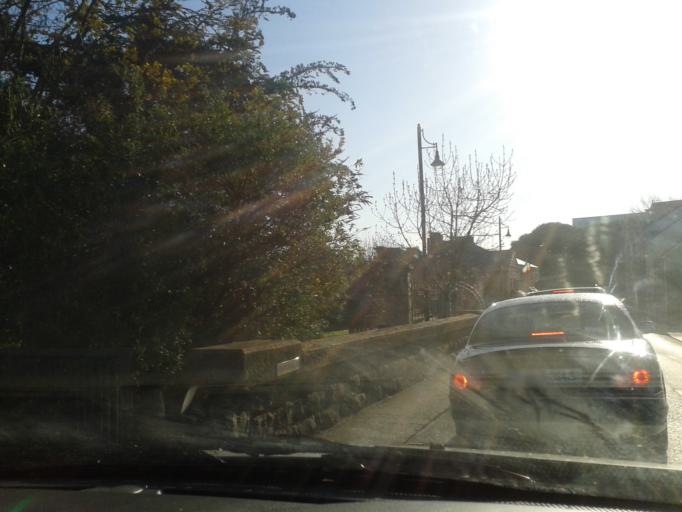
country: IE
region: Leinster
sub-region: Fingal County
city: Swords
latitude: 53.4594
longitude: -6.2224
